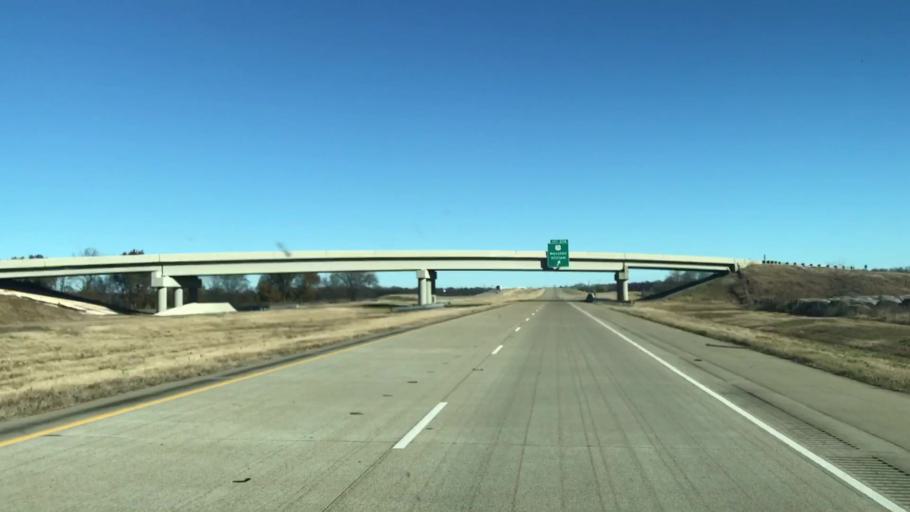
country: US
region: Louisiana
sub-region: Caddo Parish
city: Vivian
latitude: 32.8447
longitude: -93.8680
